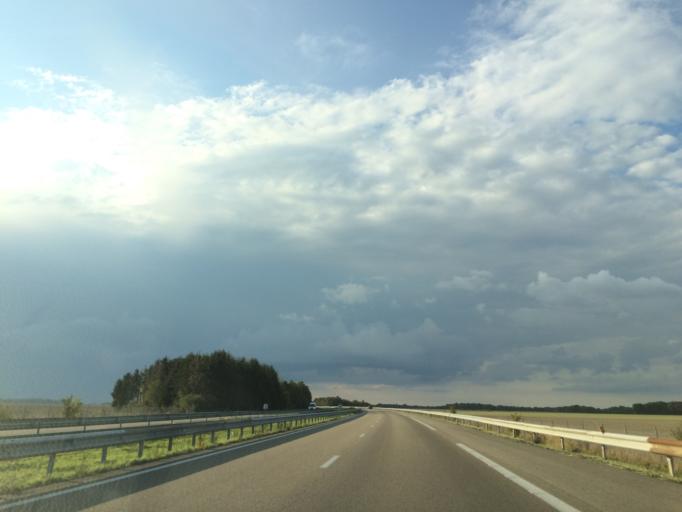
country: FR
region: Bourgogne
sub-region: Departement de l'Yonne
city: Cheroy
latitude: 48.1269
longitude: 2.9649
